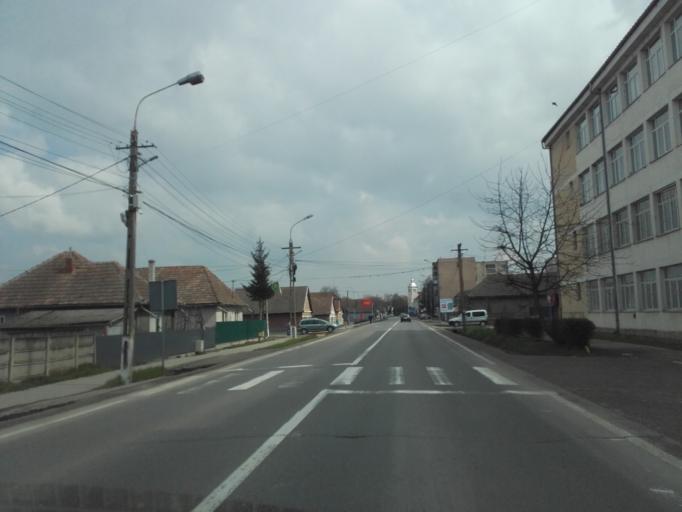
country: RO
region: Mures
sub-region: Comuna Iernut
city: Iernut
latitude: 46.4496
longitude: 24.2279
